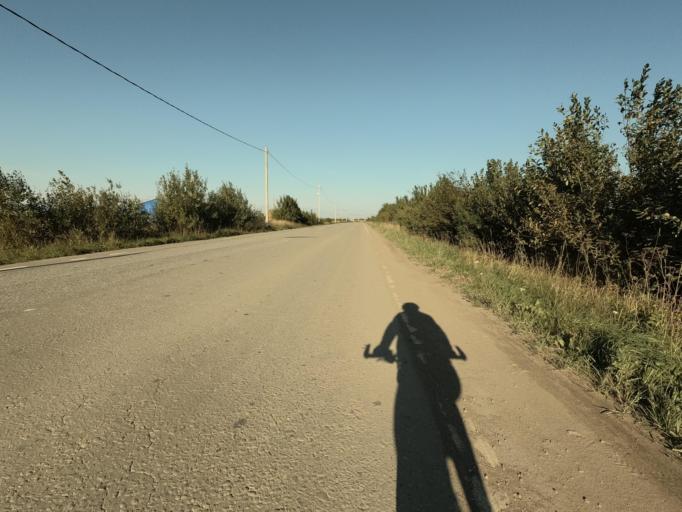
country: RU
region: St.-Petersburg
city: Petro-Slavyanka
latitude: 59.7659
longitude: 30.4875
